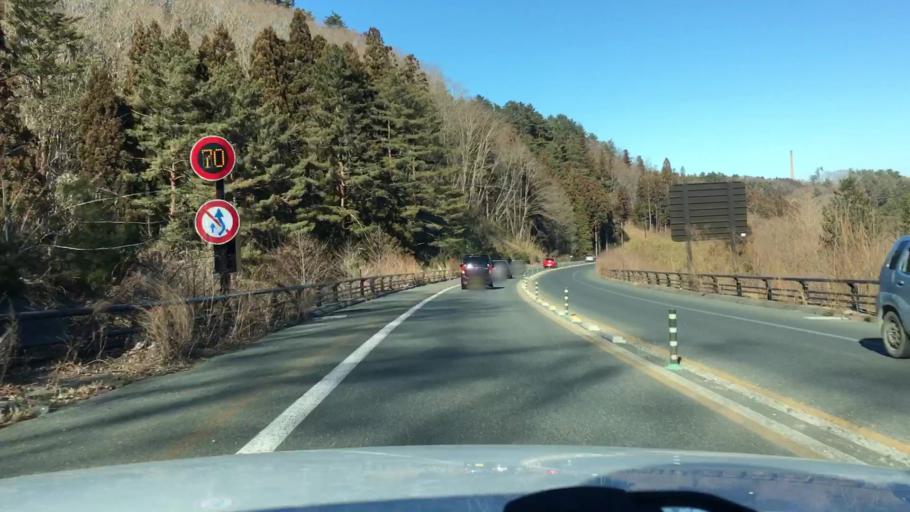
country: JP
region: Iwate
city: Miyako
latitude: 39.6063
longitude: 141.9311
